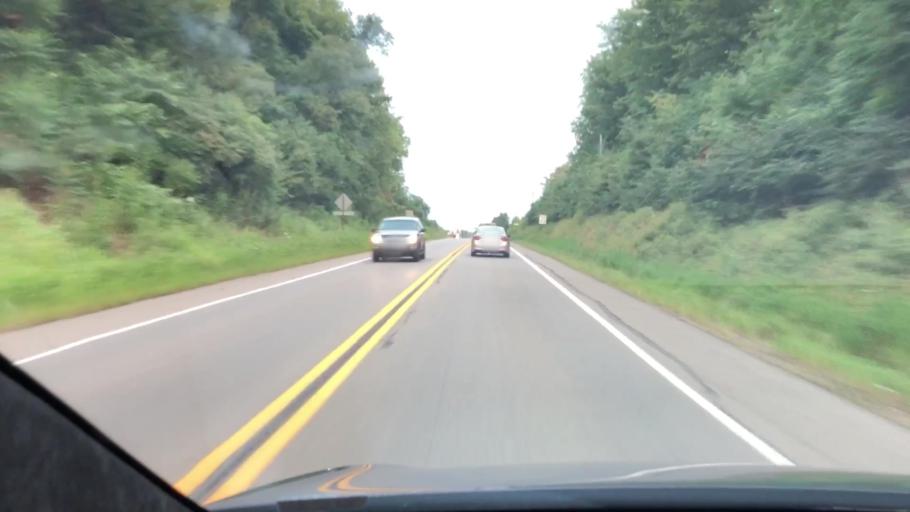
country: US
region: Pennsylvania
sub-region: Butler County
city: Shanor-Northvue
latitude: 40.9116
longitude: -79.9337
